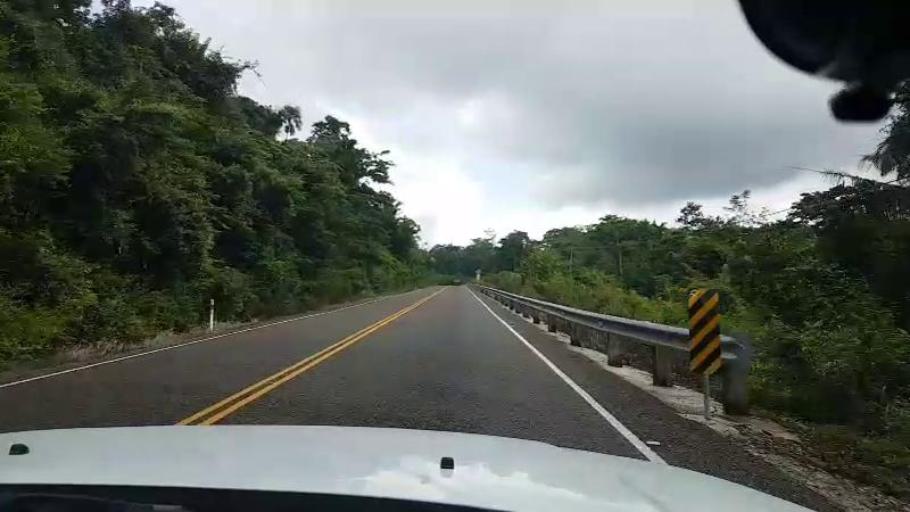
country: BZ
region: Cayo
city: Belmopan
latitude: 17.1548
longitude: -88.6794
